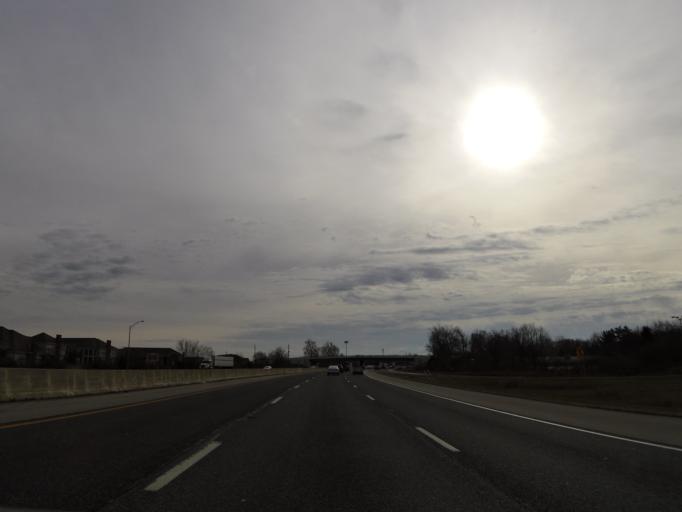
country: US
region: Indiana
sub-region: Marion County
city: Lawrence
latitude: 39.8932
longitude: -86.0519
